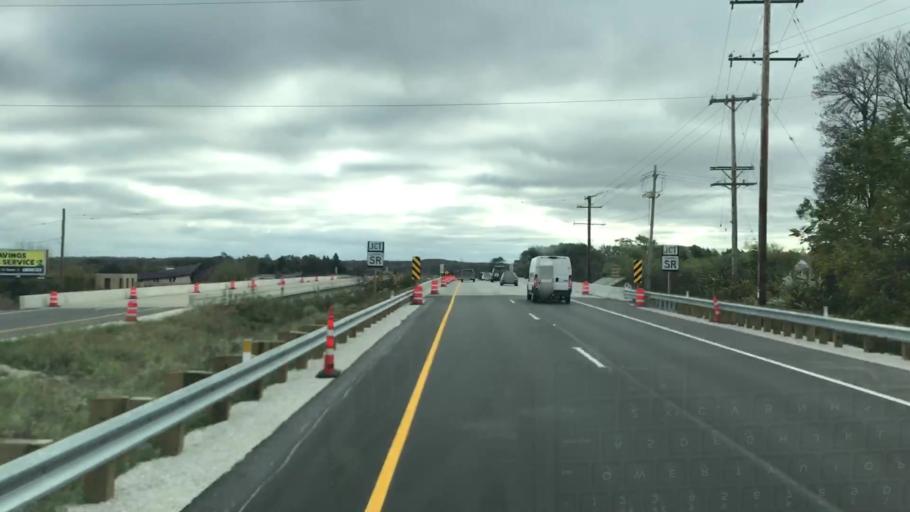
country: US
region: Wisconsin
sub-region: Waukesha County
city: Sussex
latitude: 43.0826
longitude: -88.1934
